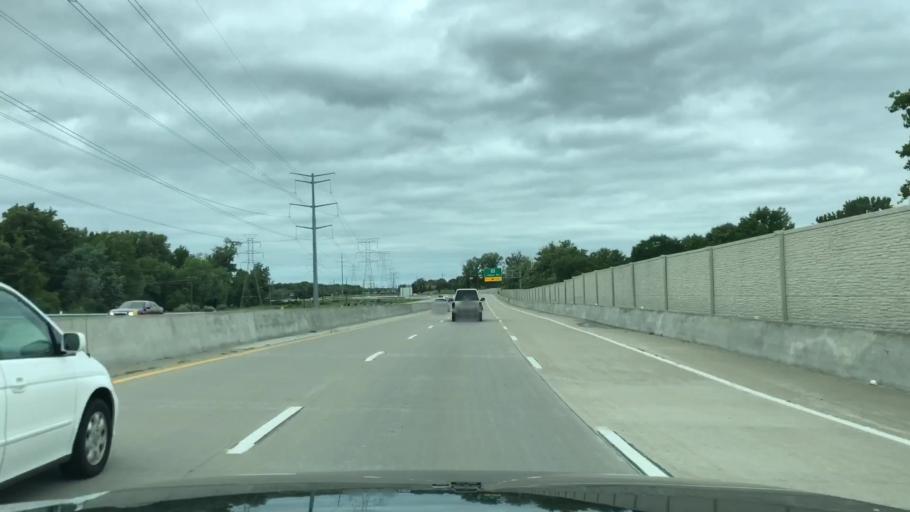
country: US
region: Missouri
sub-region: Saint Louis County
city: Town and Country
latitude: 38.6697
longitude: -90.4967
